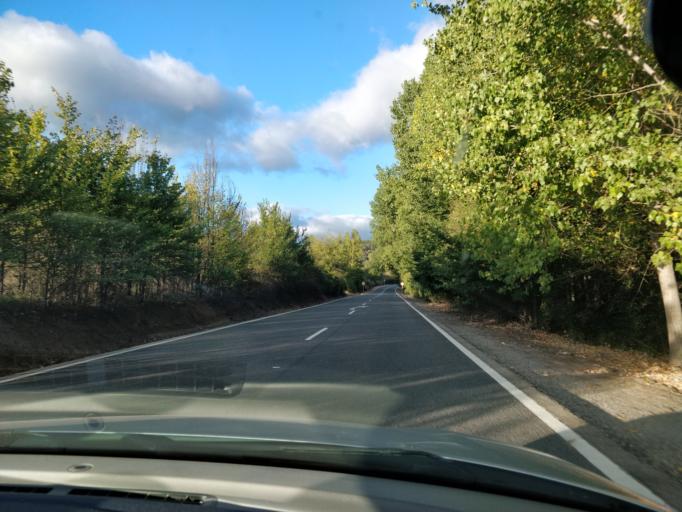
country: ES
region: Castille and Leon
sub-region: Provincia de Leon
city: Borrenes
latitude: 42.4978
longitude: -6.7343
